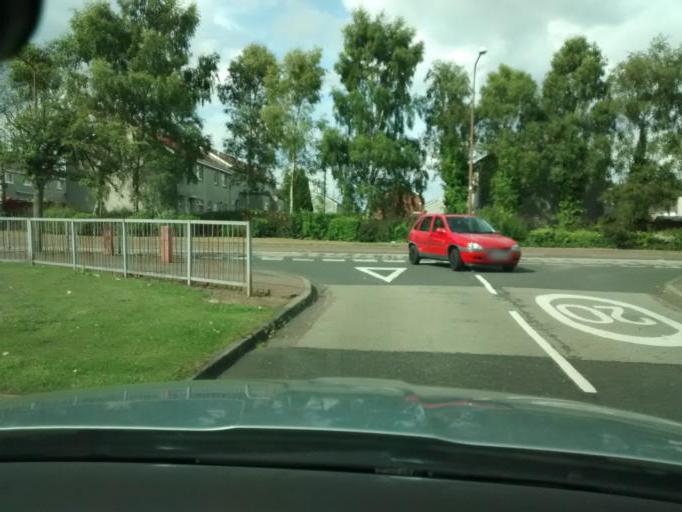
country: GB
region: Scotland
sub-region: West Lothian
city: Livingston
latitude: 55.8978
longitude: -3.5161
